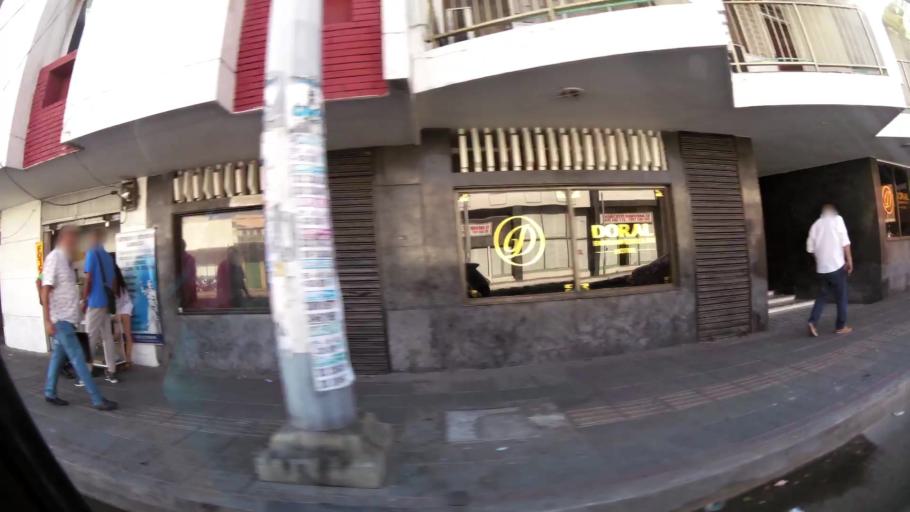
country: CO
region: Atlantico
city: Barranquilla
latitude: 10.9851
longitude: -74.7855
